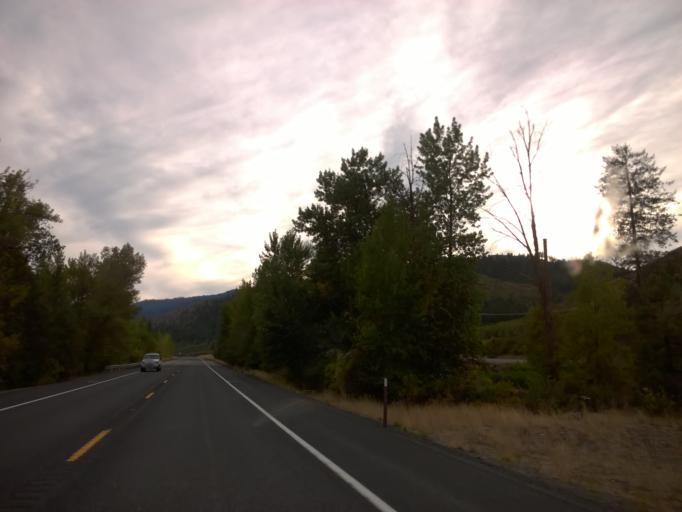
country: US
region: Washington
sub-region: Chelan County
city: Leavenworth
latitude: 47.5476
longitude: -120.6122
